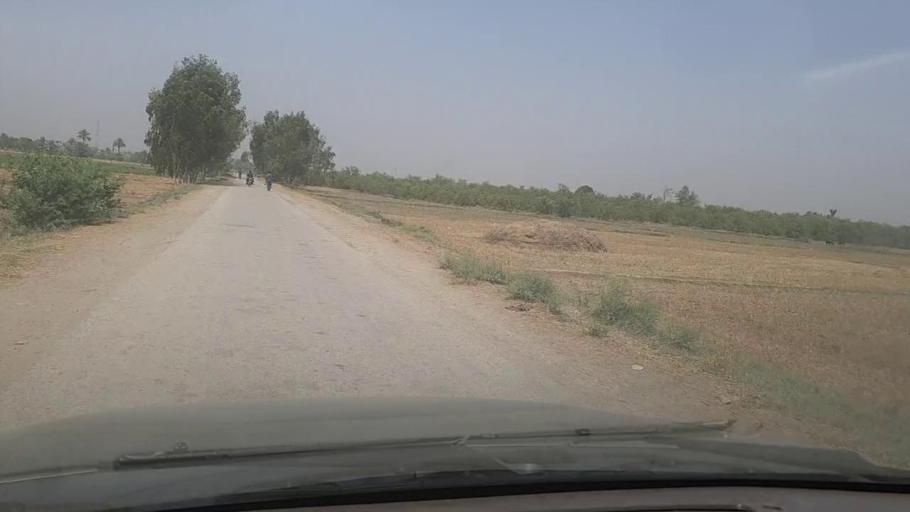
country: PK
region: Sindh
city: Madeji
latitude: 27.7982
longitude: 68.4176
